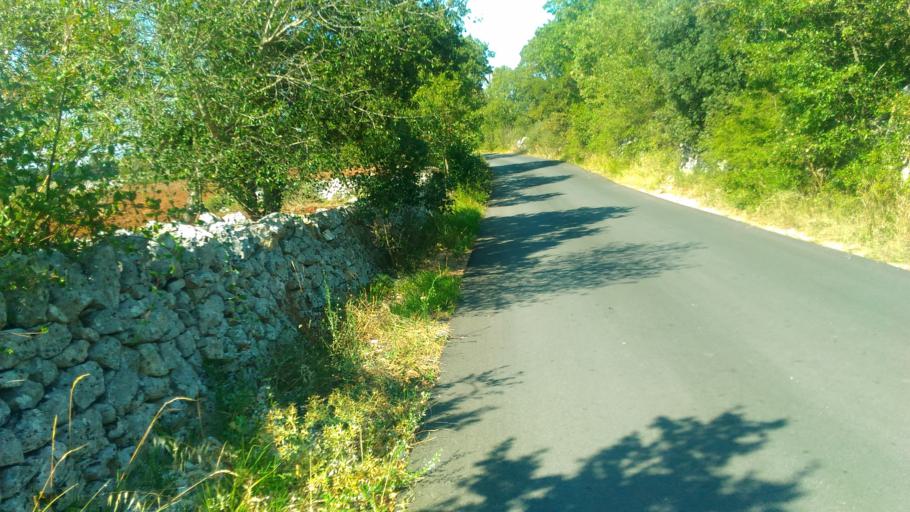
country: IT
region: Apulia
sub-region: Provincia di Bari
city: Noci
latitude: 40.8073
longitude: 17.1822
